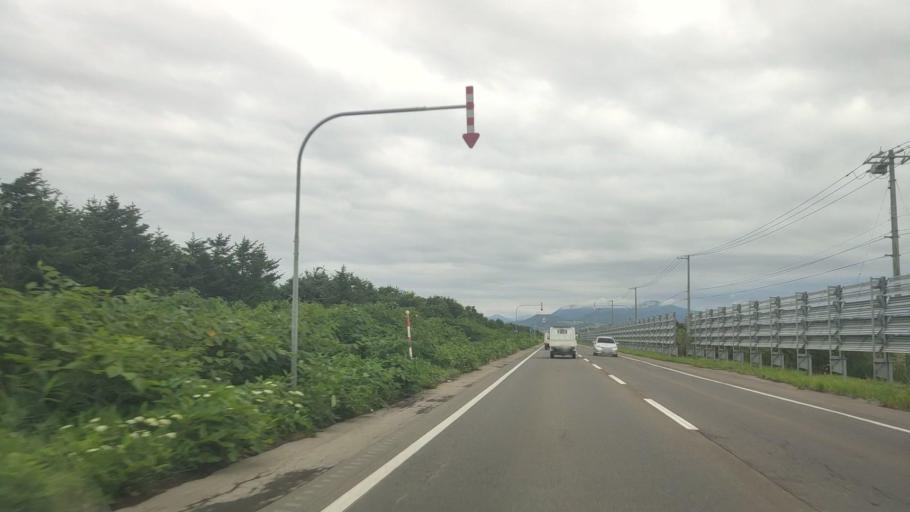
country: JP
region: Hokkaido
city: Nanae
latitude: 42.2976
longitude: 140.2719
